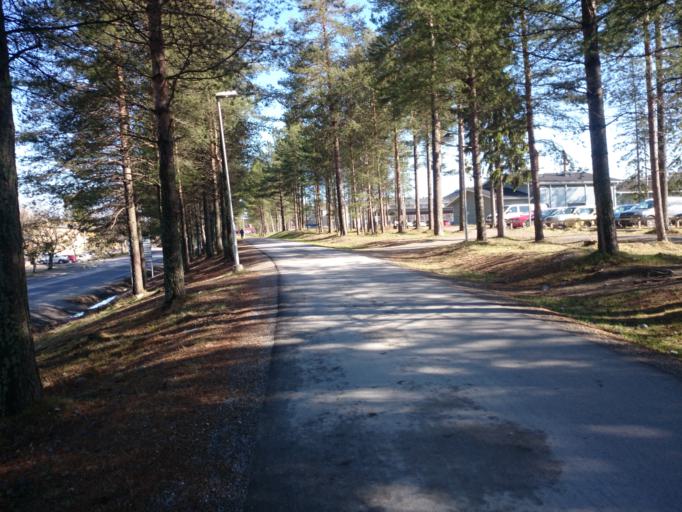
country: SE
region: Vaesterbotten
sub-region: Umea Kommun
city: Umea
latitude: 63.8163
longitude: 20.3044
